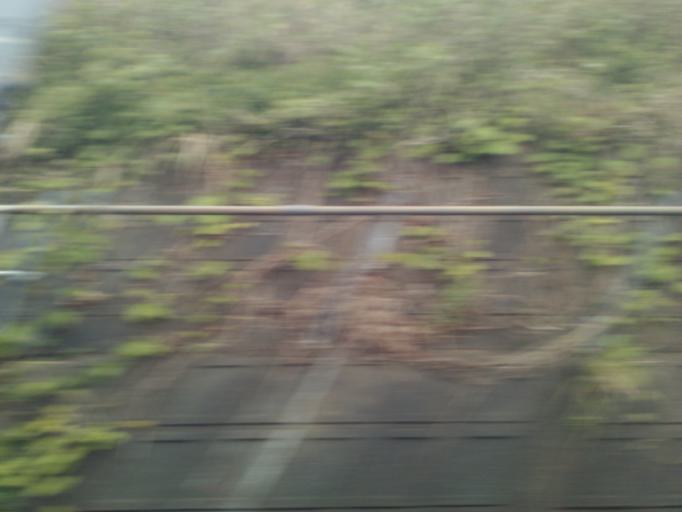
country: JP
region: Kanagawa
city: Yokohama
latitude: 35.4861
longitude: 139.5848
